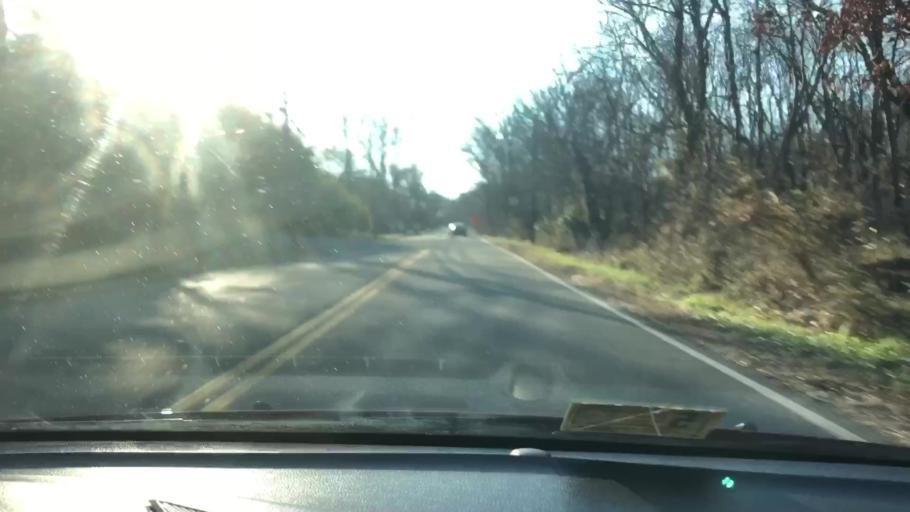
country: US
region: Virginia
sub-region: Fairfax County
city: Rose Hill
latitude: 38.7846
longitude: -77.0973
